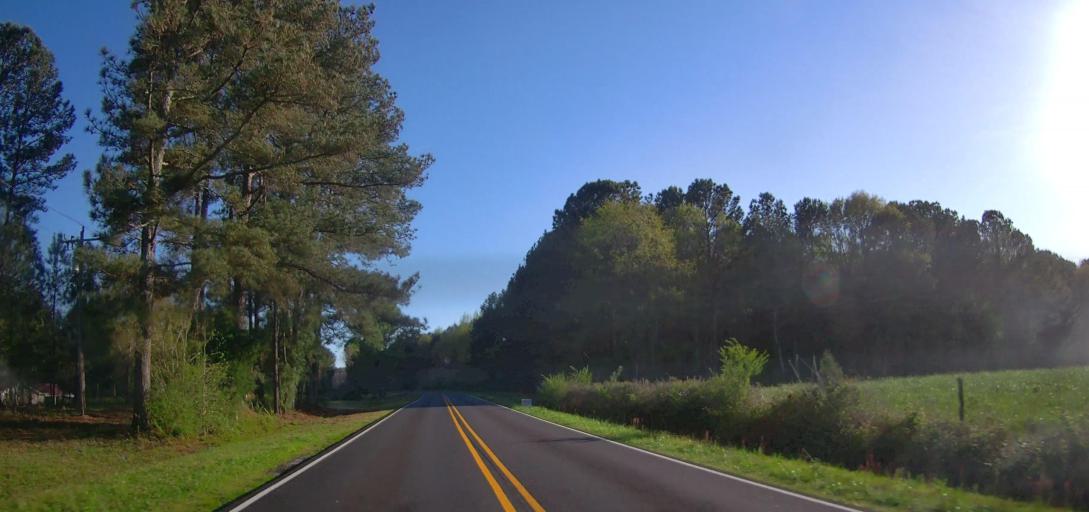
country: US
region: Georgia
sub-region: Butts County
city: Jackson
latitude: 33.3424
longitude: -83.9099
